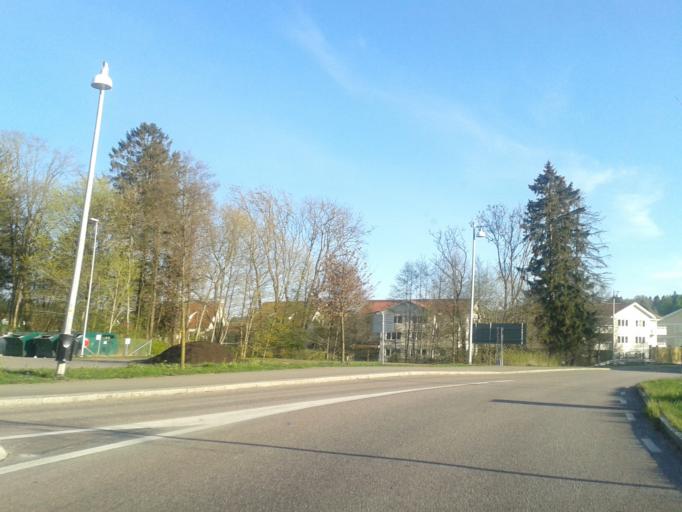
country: SE
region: Vaestra Goetaland
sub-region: Ale Kommun
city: Nodinge-Nol
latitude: 57.8919
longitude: 12.0459
